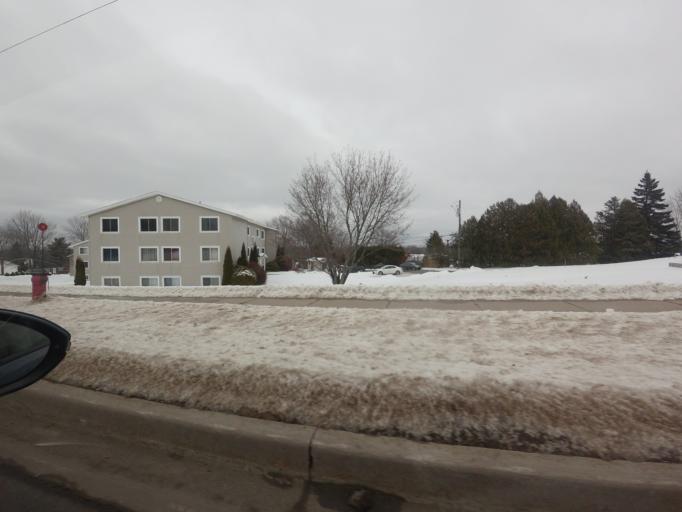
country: CA
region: New Brunswick
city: Oromocto
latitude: 45.8492
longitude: -66.4906
